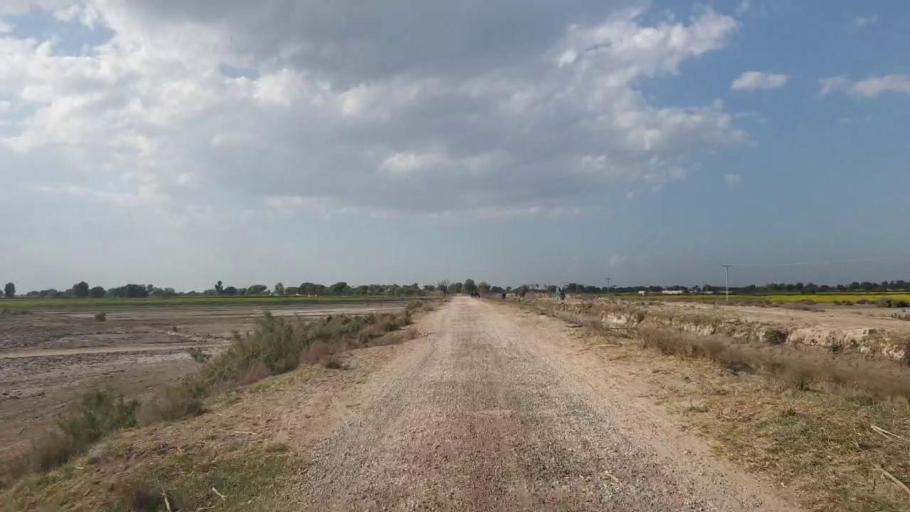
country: PK
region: Sindh
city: Shahdadpur
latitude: 26.0336
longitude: 68.4826
